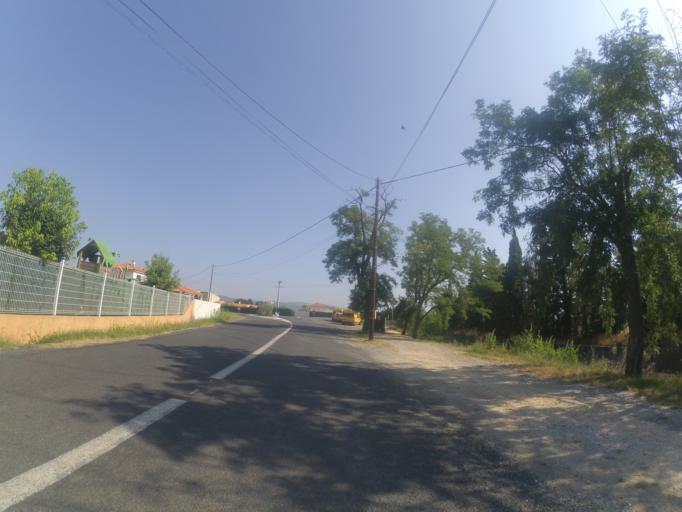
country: FR
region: Languedoc-Roussillon
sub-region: Departement des Pyrenees-Orientales
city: Ille-sur-Tet
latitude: 42.6549
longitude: 2.6235
